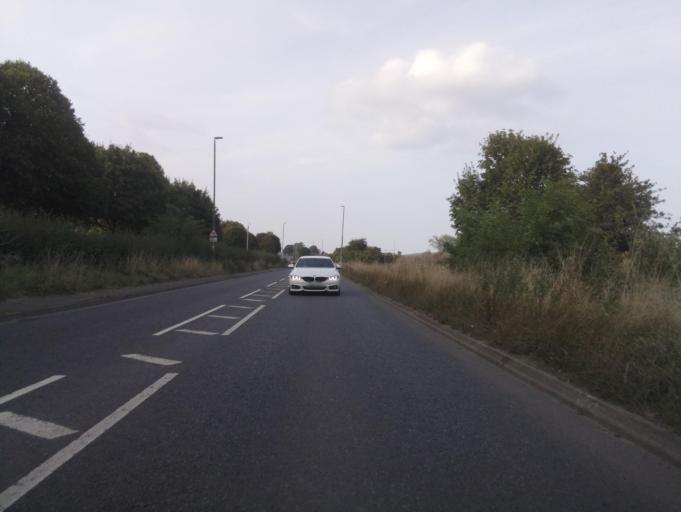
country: GB
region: England
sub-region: Gloucestershire
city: Gotherington
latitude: 51.9349
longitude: -2.0656
